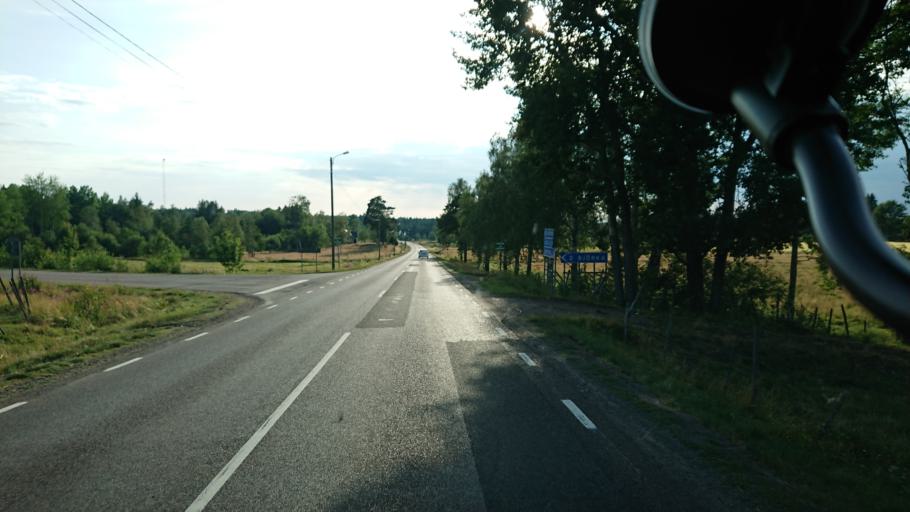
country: SE
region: Kronoberg
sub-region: Vaxjo Kommun
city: Braas
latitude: 57.0227
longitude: 15.0267
